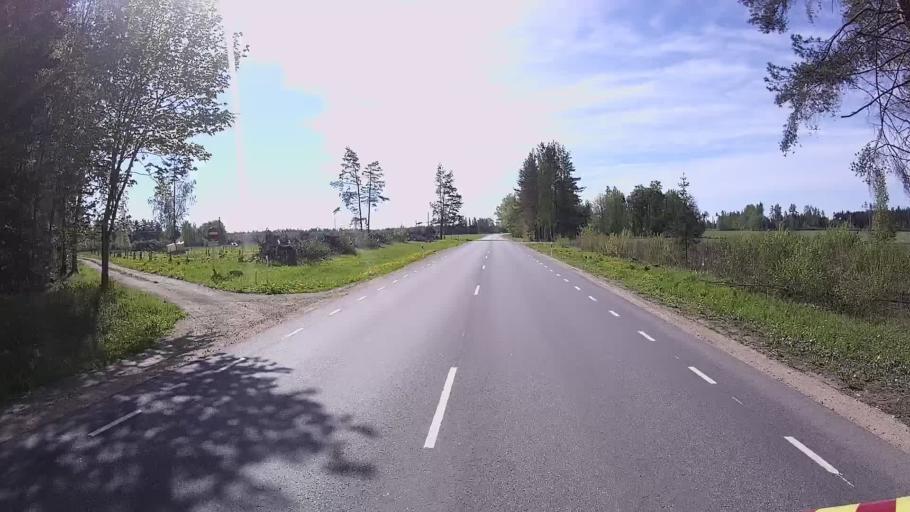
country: EE
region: Polvamaa
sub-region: Polva linn
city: Polva
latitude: 58.3130
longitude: 26.9918
